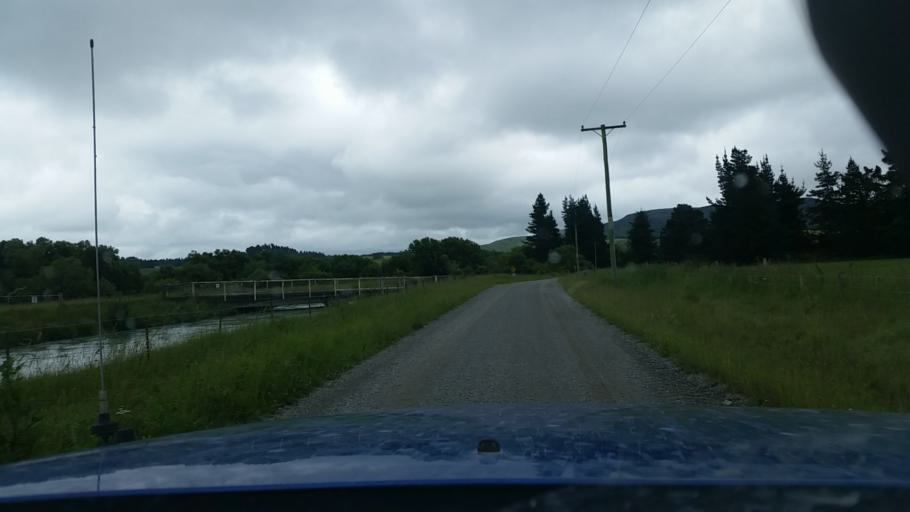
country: NZ
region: Canterbury
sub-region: Ashburton District
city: Methven
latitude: -43.6672
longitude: 171.4313
